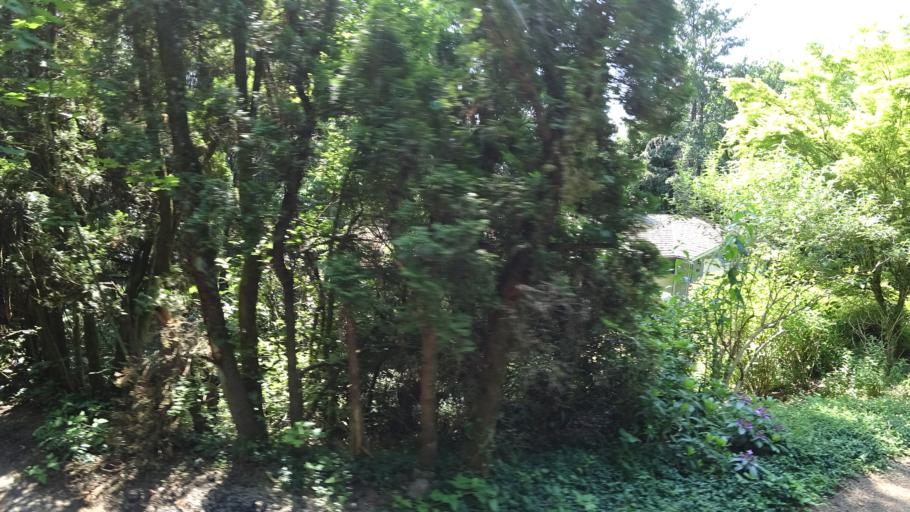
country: US
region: Oregon
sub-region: Clackamas County
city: Happy Valley
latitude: 45.4459
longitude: -122.5543
